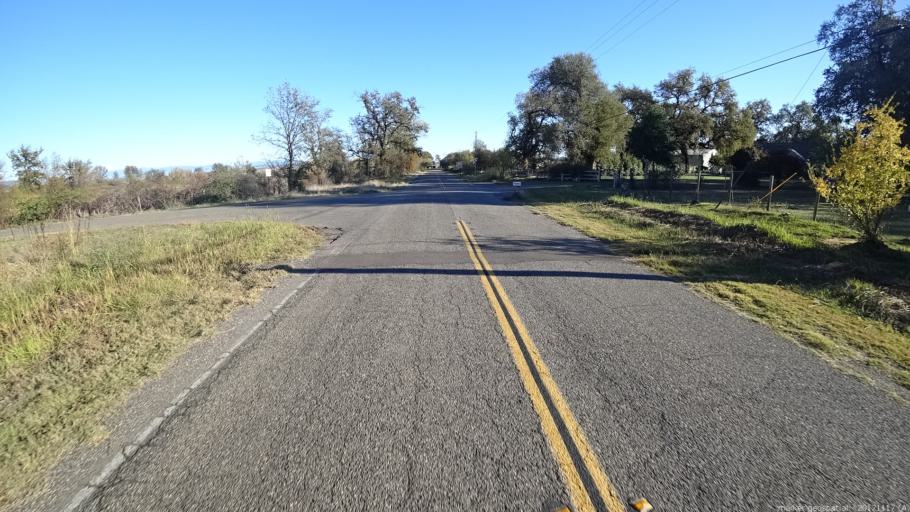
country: US
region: California
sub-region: Shasta County
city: Cottonwood
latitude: 40.3946
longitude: -122.2173
